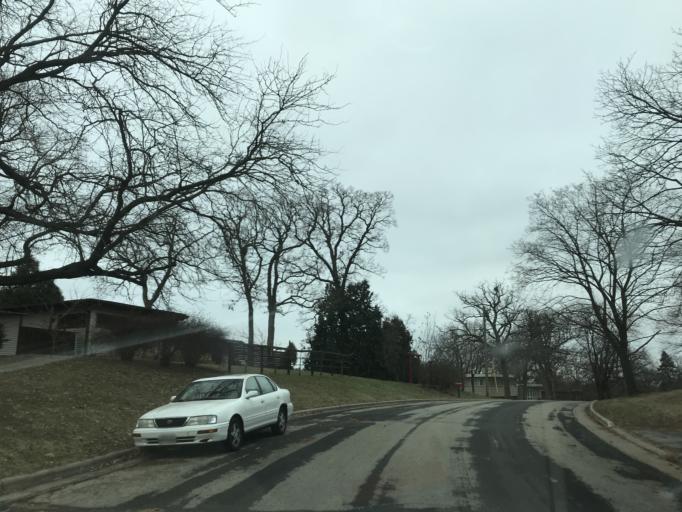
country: US
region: Wisconsin
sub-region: Dane County
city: Monona
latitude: 43.0522
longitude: -89.3267
